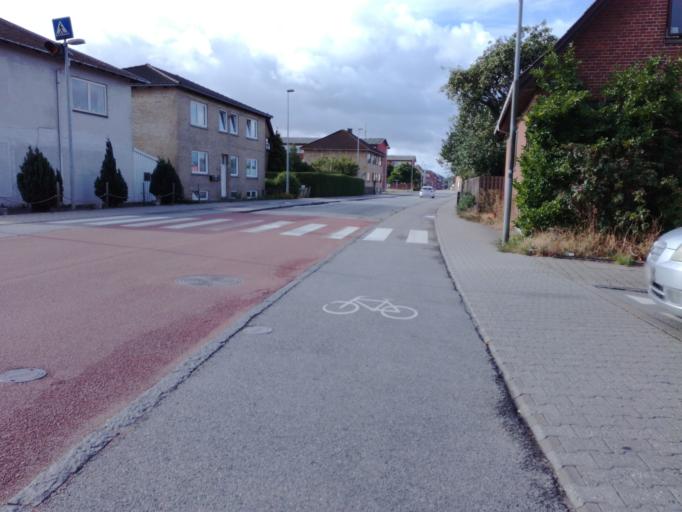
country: DK
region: South Denmark
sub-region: Fredericia Kommune
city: Fredericia
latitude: 55.5777
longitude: 9.7608
